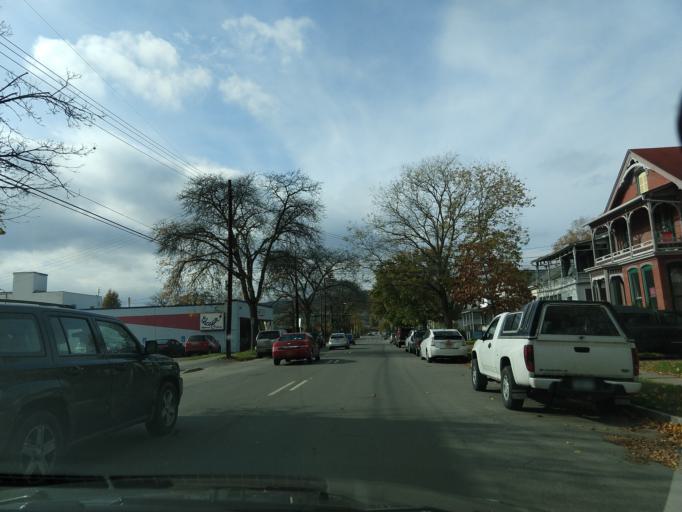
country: US
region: New York
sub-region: Tompkins County
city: Ithaca
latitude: 42.4403
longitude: -76.5048
